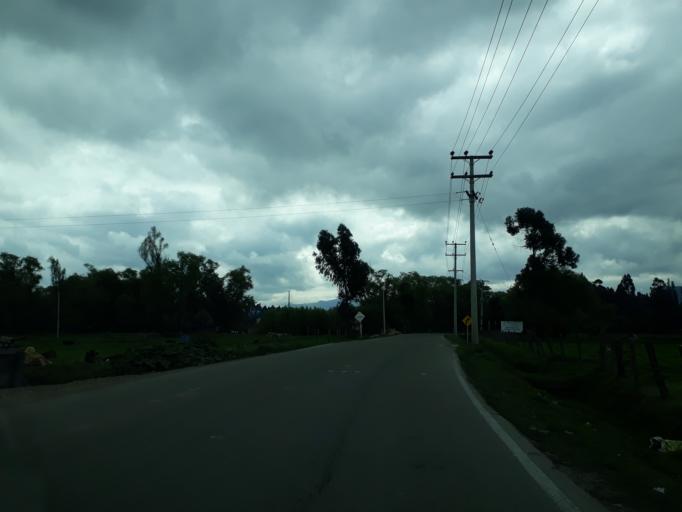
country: CO
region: Cundinamarca
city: Ubate
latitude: 5.3209
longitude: -73.7956
